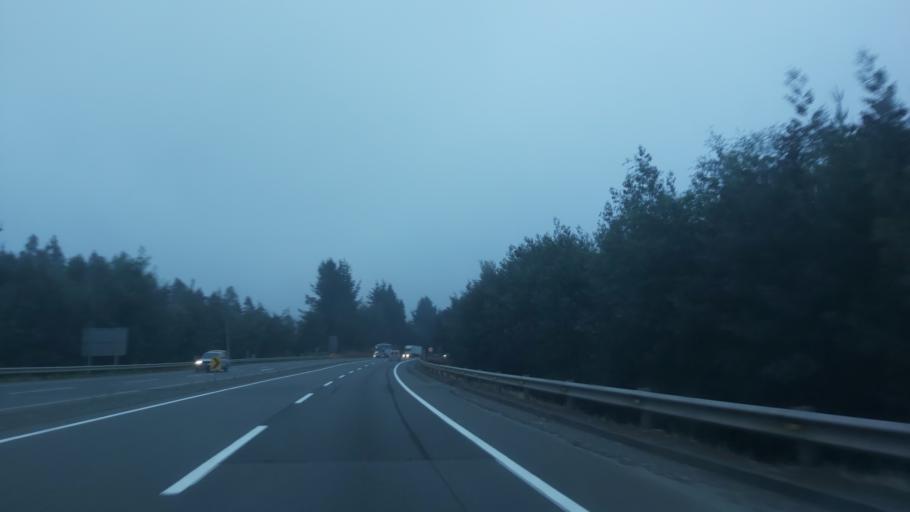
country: CL
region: Biobio
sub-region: Provincia de Concepcion
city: Penco
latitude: -36.7376
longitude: -72.8922
